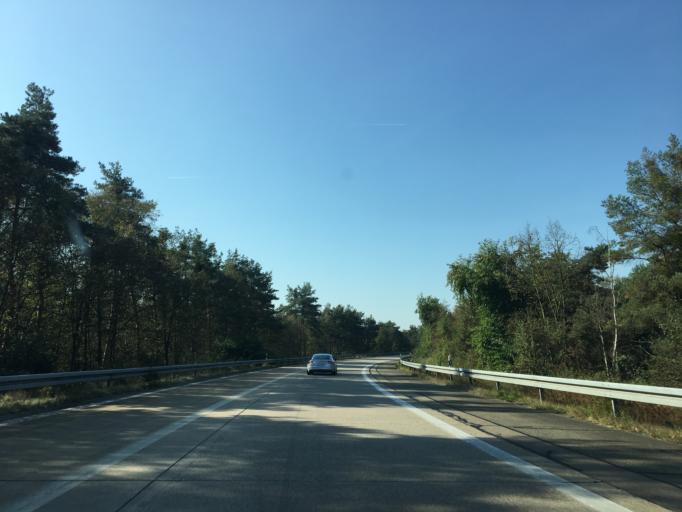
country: DE
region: Baden-Wuerttemberg
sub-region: Karlsruhe Region
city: Hockenheim
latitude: 49.3350
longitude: 8.5569
